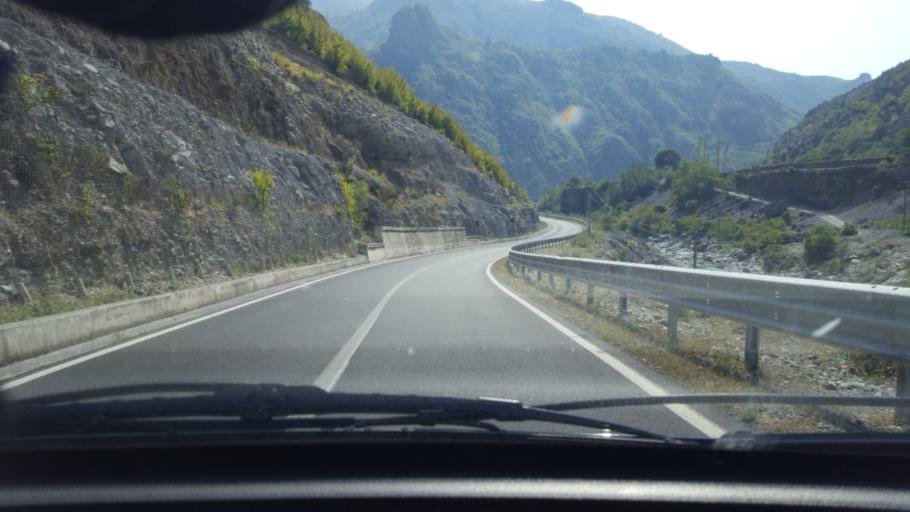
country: AL
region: Shkoder
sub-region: Rrethi i Malesia e Madhe
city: Kastrat
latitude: 42.4607
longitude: 19.5613
